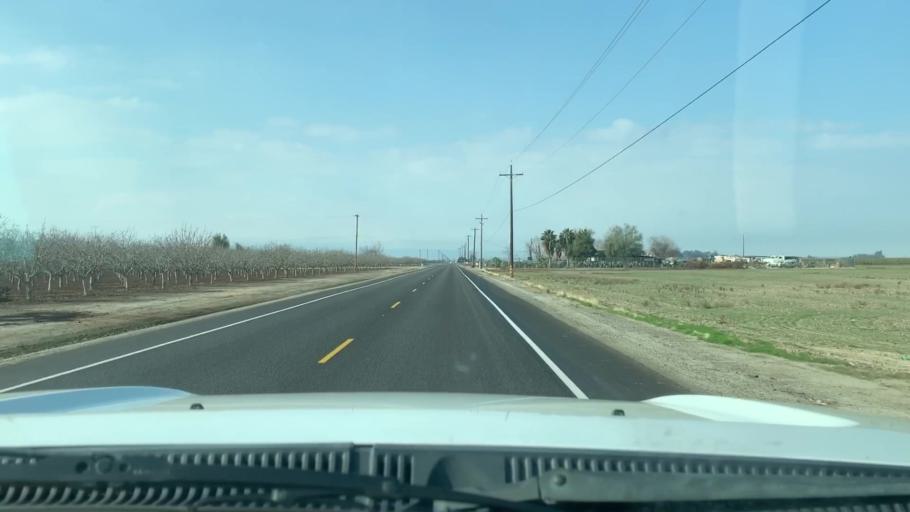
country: US
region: California
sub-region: Kern County
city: Buttonwillow
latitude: 35.4422
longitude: -119.4048
